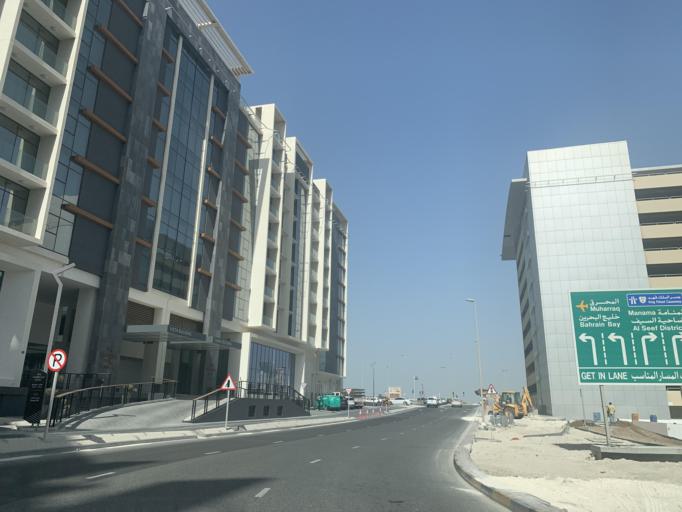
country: BH
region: Manama
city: Manama
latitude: 26.2393
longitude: 50.5740
